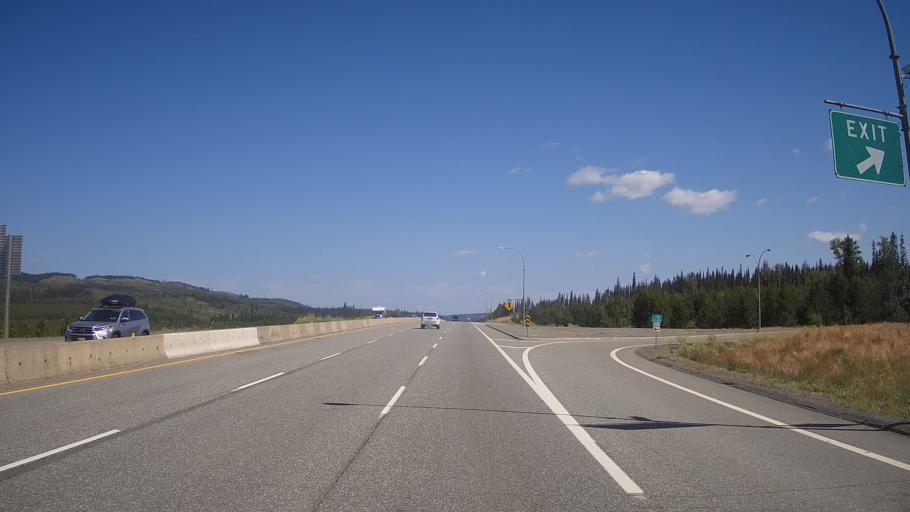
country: CA
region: British Columbia
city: Logan Lake
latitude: 50.3207
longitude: -120.6372
